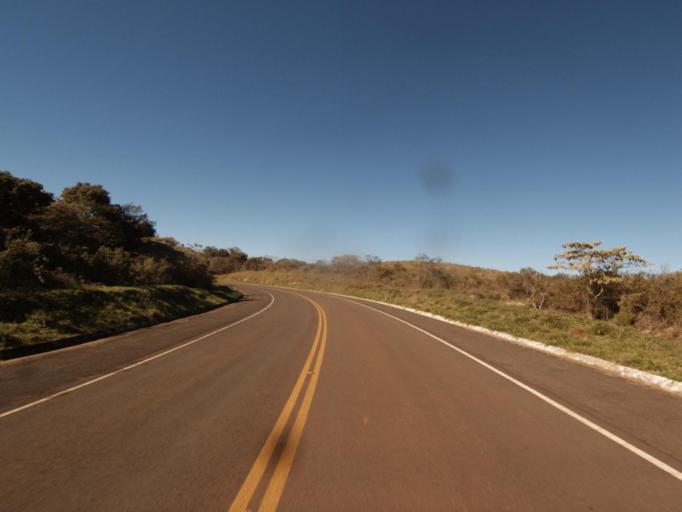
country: AR
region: Misiones
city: Bernardo de Irigoyen
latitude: -26.6136
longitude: -53.6972
